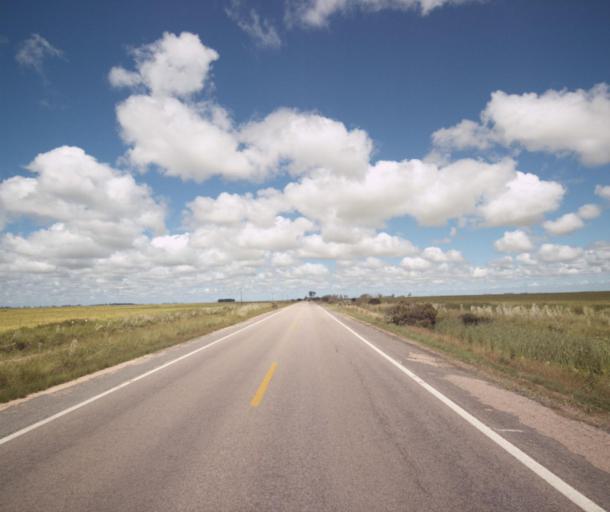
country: BR
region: Rio Grande do Sul
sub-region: Rio Grande
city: Rio Grande
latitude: -32.1672
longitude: -52.4089
